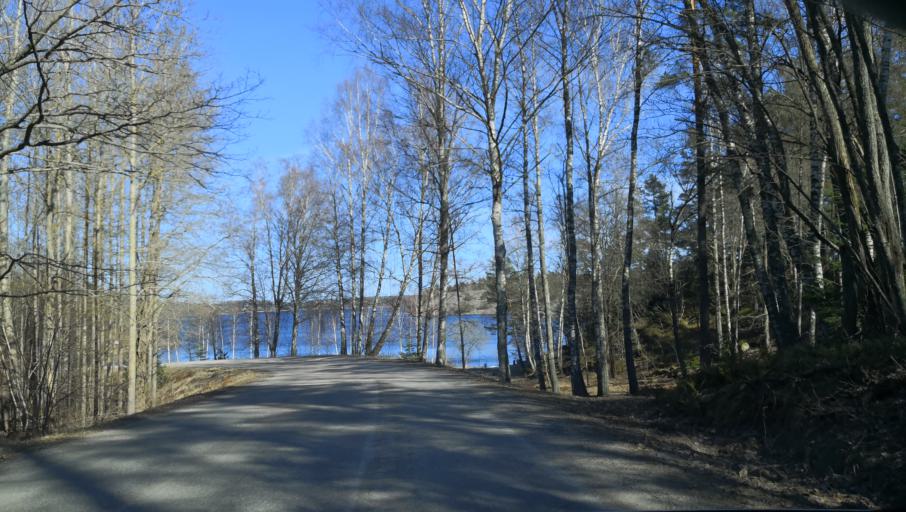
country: SE
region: Stockholm
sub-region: Varmdo Kommun
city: Mortnas
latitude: 59.2933
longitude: 18.4181
